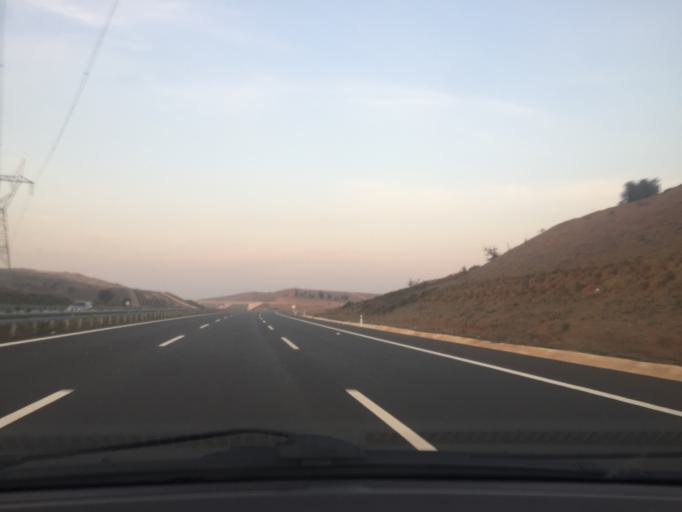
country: TR
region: Bursa
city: Mahmudiye
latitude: 40.2755
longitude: 28.5492
